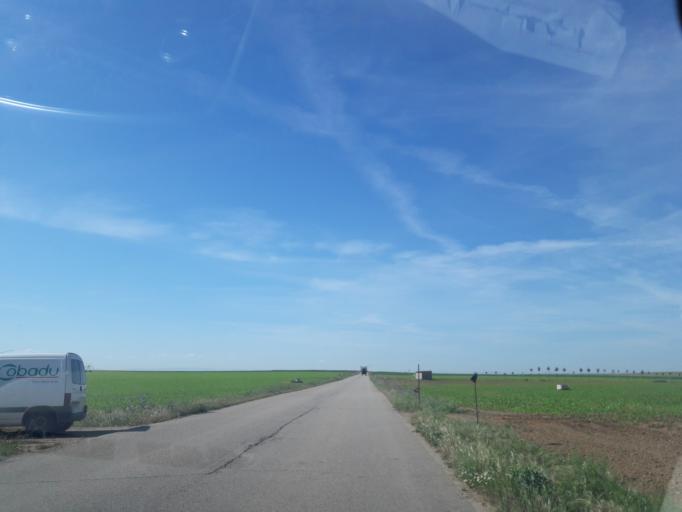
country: ES
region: Castille and Leon
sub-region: Provincia de Salamanca
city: Villoruela
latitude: 41.0244
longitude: -5.3922
